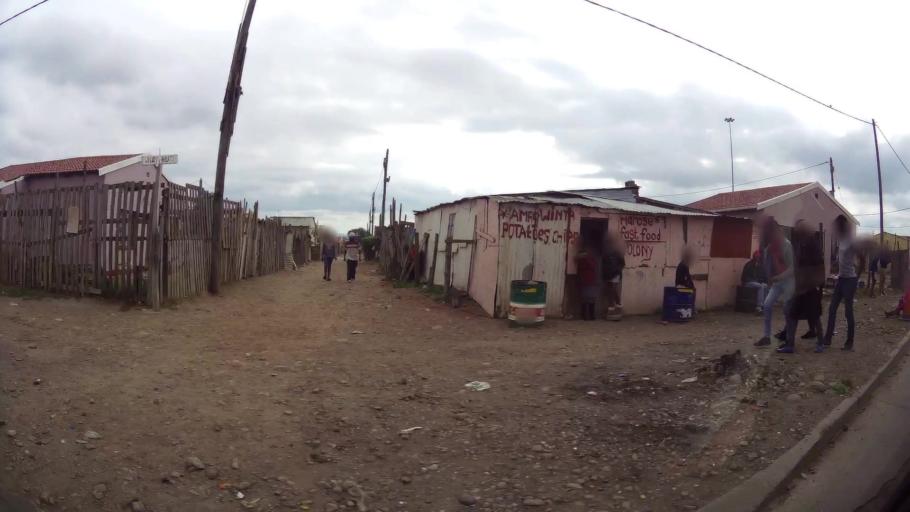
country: ZA
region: Eastern Cape
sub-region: Nelson Mandela Bay Metropolitan Municipality
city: Port Elizabeth
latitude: -33.8657
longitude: 25.5731
